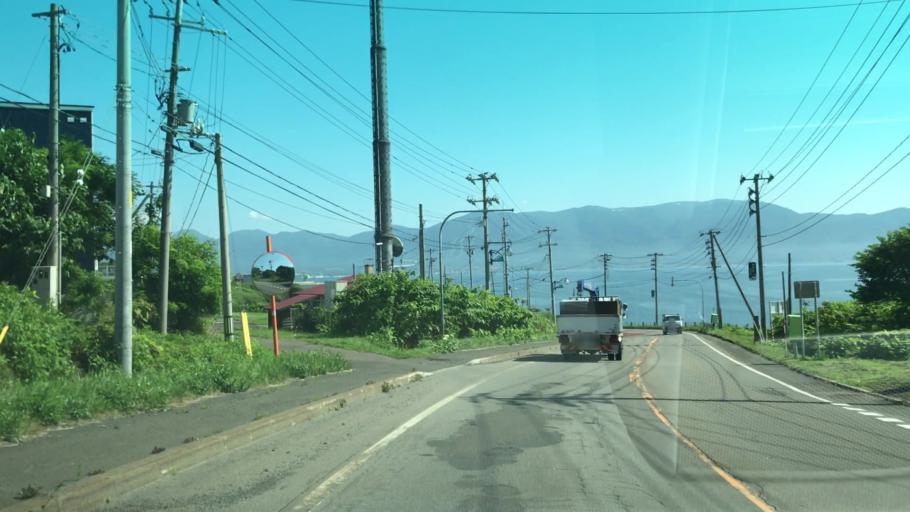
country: JP
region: Hokkaido
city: Iwanai
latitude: 43.0582
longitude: 140.4984
